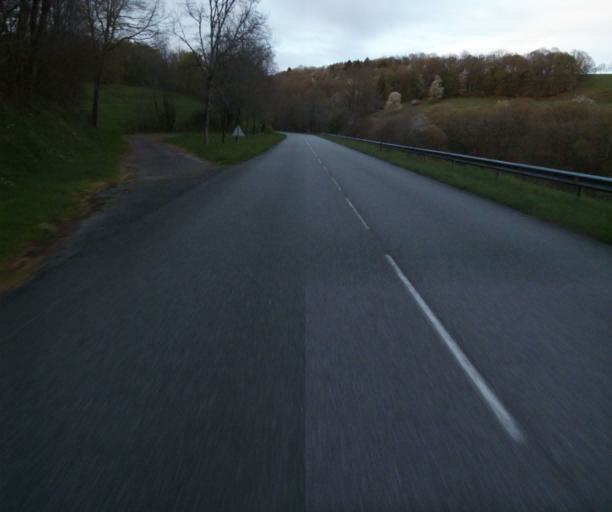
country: FR
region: Limousin
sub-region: Departement de la Correze
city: Laguenne
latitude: 45.2528
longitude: 1.8015
